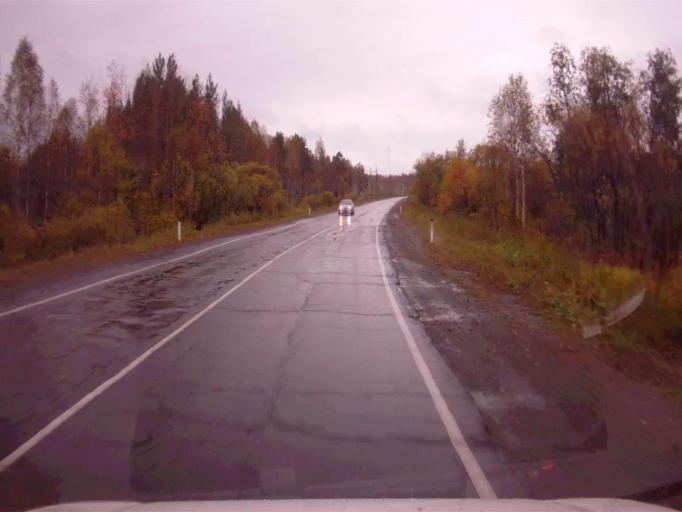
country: RU
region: Chelyabinsk
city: Verkhniy Ufaley
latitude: 55.9896
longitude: 60.3347
